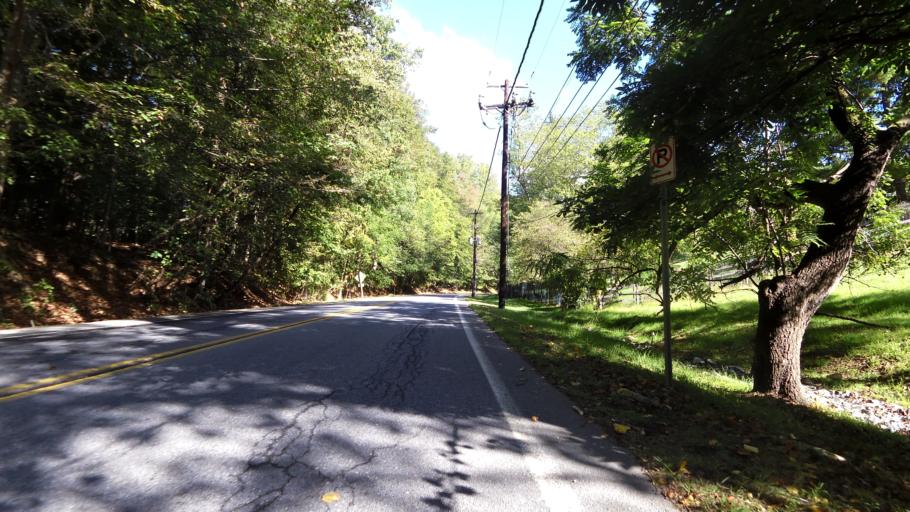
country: US
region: Maryland
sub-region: Montgomery County
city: Potomac
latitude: 38.9833
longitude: -77.2268
